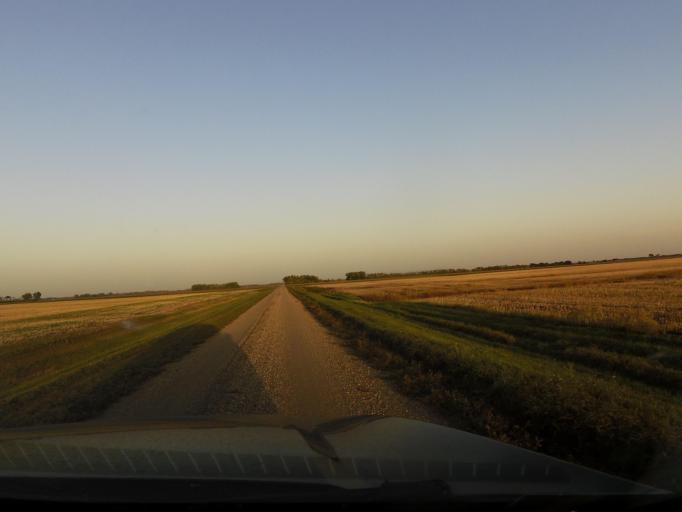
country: US
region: North Dakota
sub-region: Walsh County
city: Grafton
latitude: 48.3832
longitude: -97.2175
